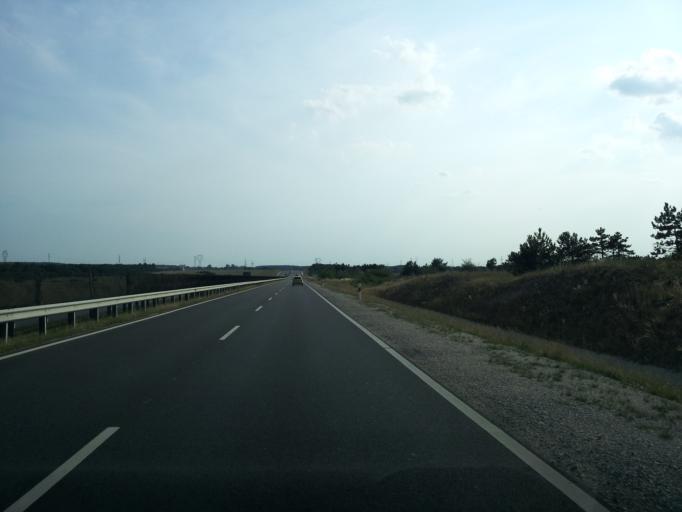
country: HU
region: Veszprem
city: Liter
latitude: 47.1248
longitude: 17.9993
